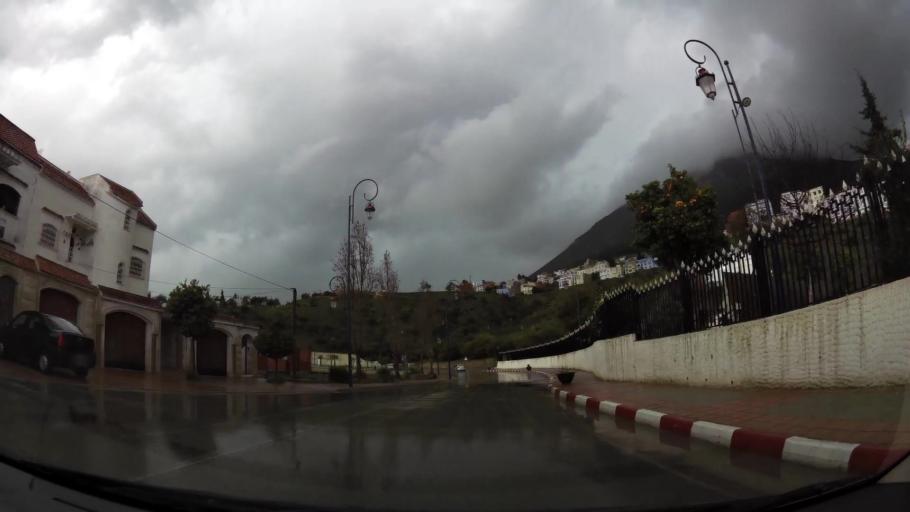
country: MA
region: Tanger-Tetouan
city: Chefchaouene
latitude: 35.1719
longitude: -5.2732
